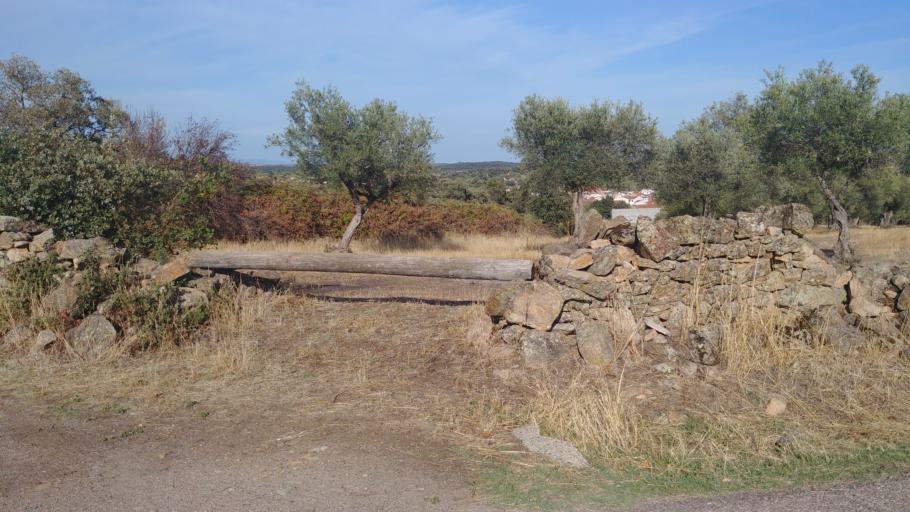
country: ES
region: Castille-La Mancha
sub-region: Province of Toledo
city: Navalcan
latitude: 40.0682
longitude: -5.1025
